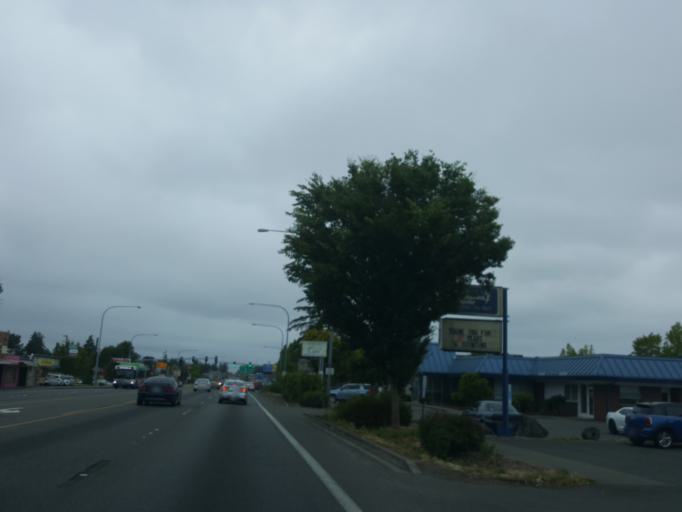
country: US
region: Washington
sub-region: Pierce County
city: Parkland
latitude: 47.1534
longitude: -122.4342
